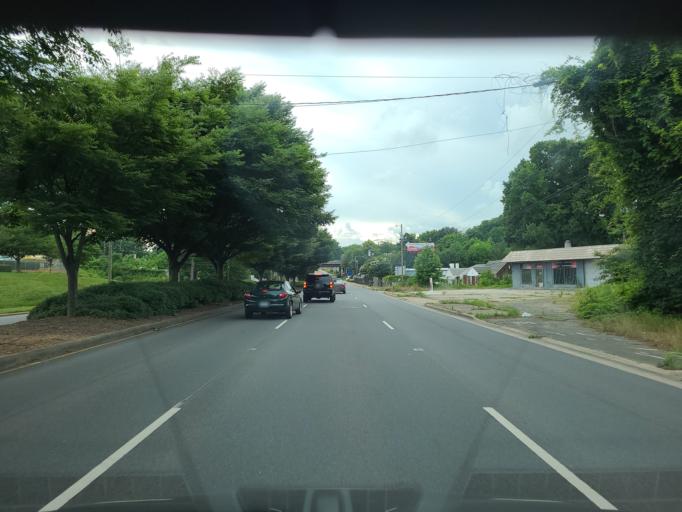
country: US
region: North Carolina
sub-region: Mecklenburg County
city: Charlotte
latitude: 35.2310
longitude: -80.9208
